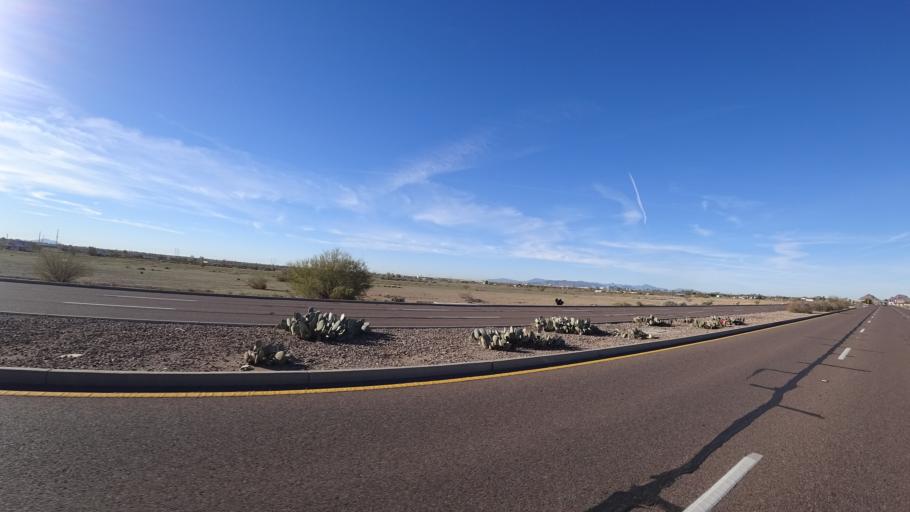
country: US
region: Arizona
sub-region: Maricopa County
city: Scottsdale
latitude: 33.4659
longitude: -111.8676
